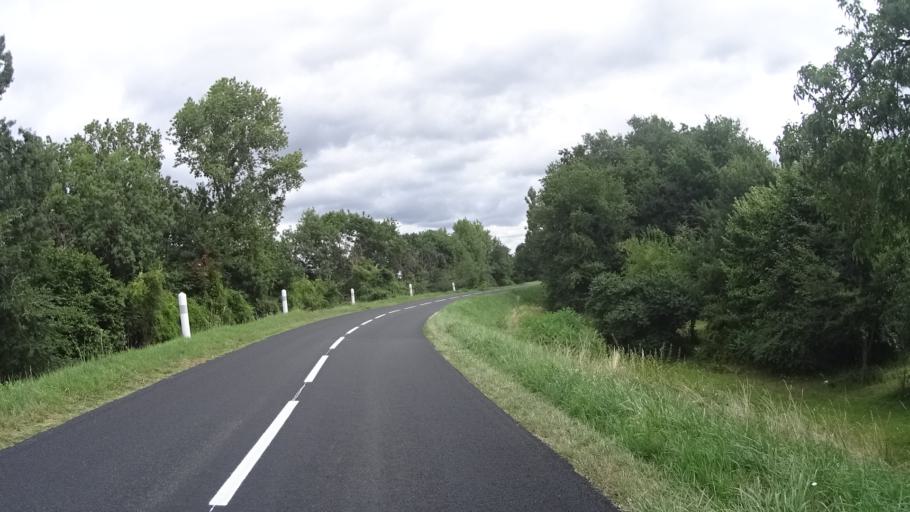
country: FR
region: Centre
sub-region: Departement d'Indre-et-Loire
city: Huismes
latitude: 47.2712
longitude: 0.3166
